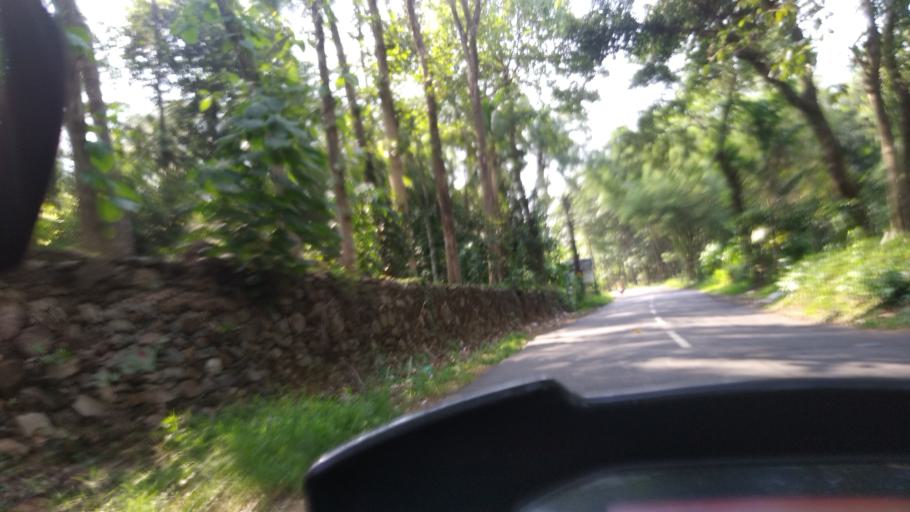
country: IN
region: Kerala
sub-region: Kottayam
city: Palackattumala
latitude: 9.8036
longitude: 76.5763
